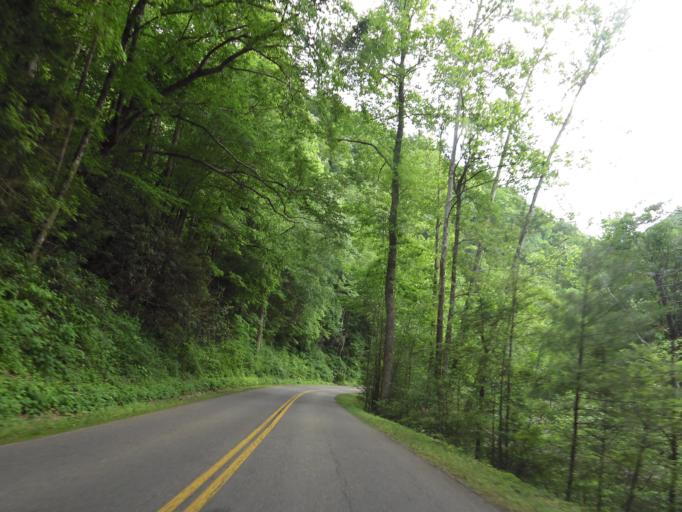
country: US
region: Tennessee
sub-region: Sevier County
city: Gatlinburg
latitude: 35.6640
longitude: -83.6304
